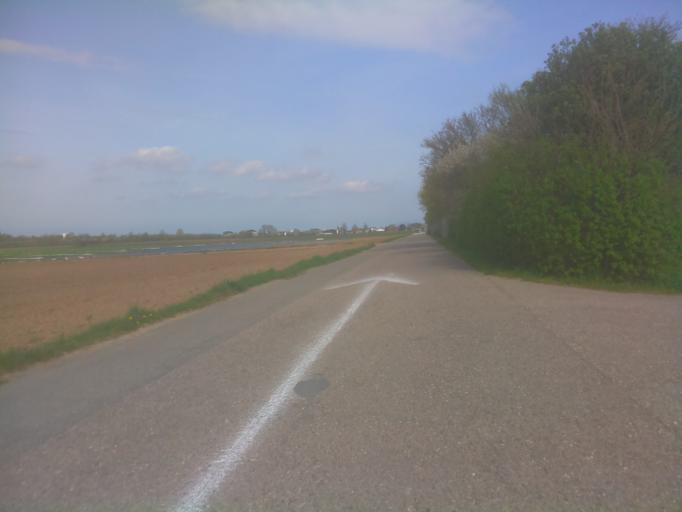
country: DE
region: Baden-Wuerttemberg
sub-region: Karlsruhe Region
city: Schriesheim
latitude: 49.5028
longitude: 8.6477
